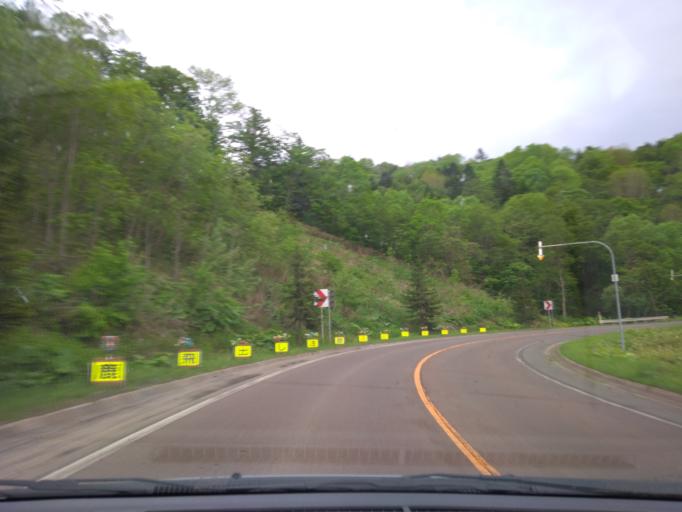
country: JP
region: Hokkaido
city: Shimo-furano
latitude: 43.0919
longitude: 142.4059
